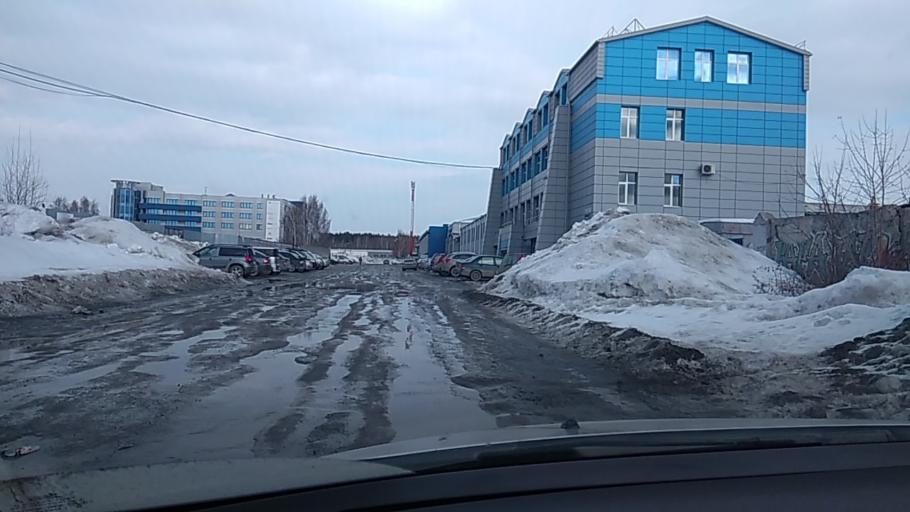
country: RU
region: Sverdlovsk
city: Yekaterinburg
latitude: 56.8625
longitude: 60.6681
